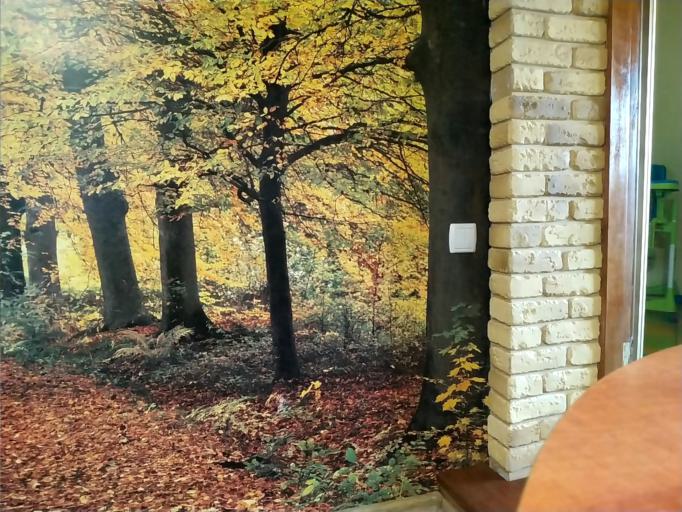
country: RU
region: Leningrad
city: Tolmachevo
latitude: 58.9465
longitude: 29.6490
